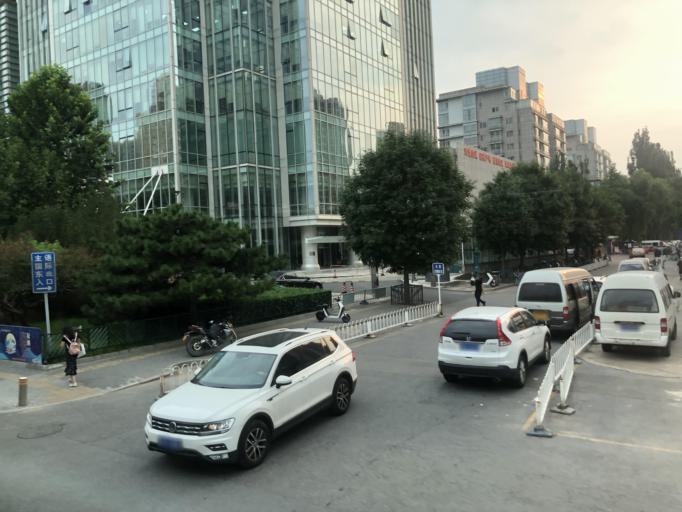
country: CN
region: Beijing
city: Jinrongjie
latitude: 39.9345
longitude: 116.3190
